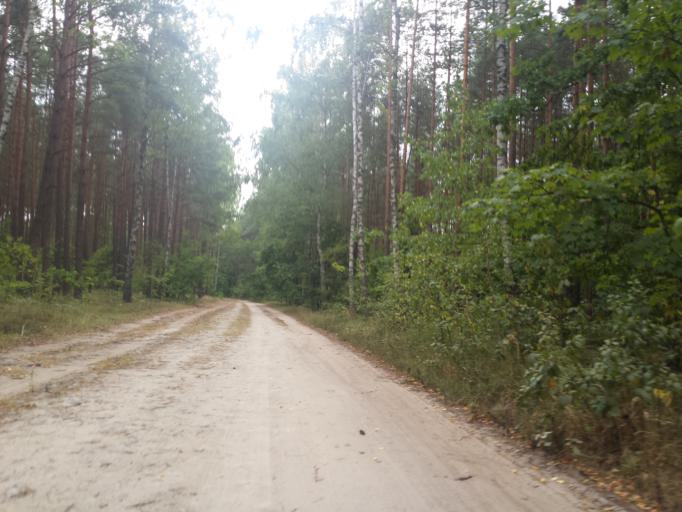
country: PL
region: Swietokrzyskie
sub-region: Powiat staszowski
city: Bogoria
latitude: 50.6574
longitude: 21.1796
